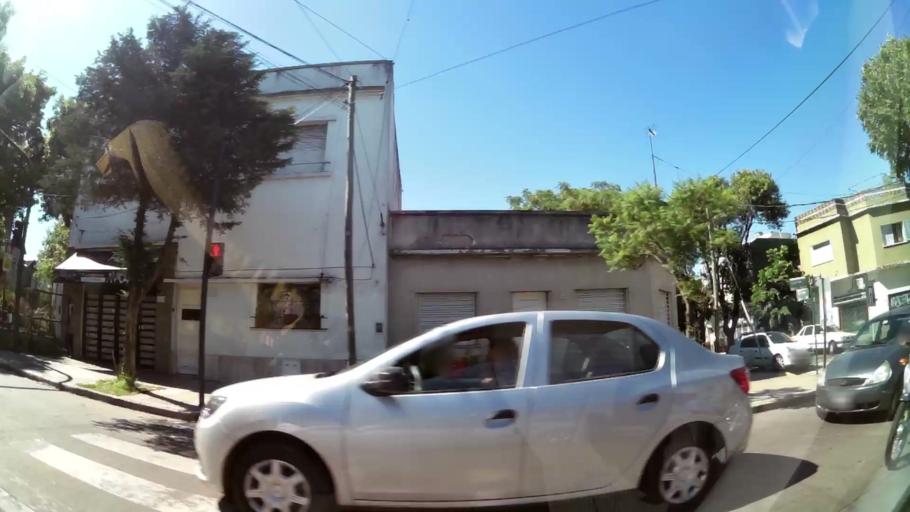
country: AR
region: Buenos Aires
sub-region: Partido de Vicente Lopez
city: Olivos
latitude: -34.5435
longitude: -58.4946
